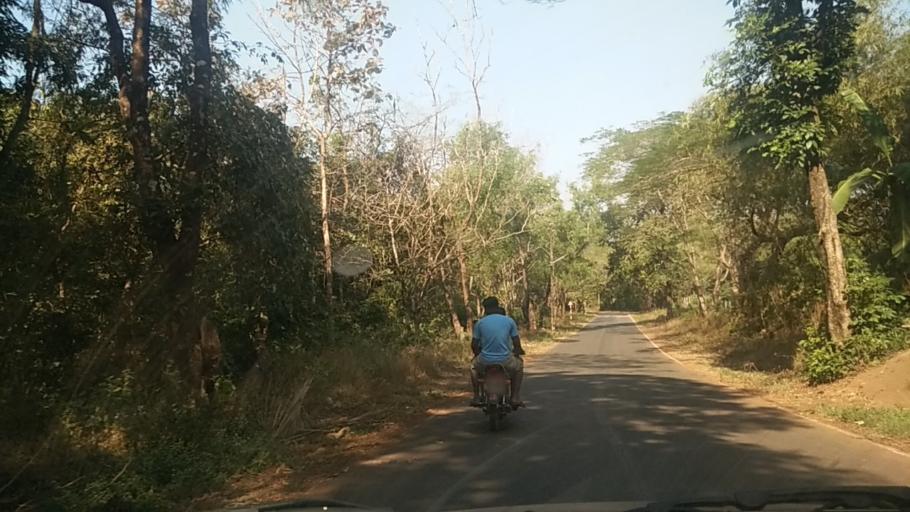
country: IN
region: Goa
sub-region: South Goa
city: Sanguem
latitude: 15.2102
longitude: 74.2166
